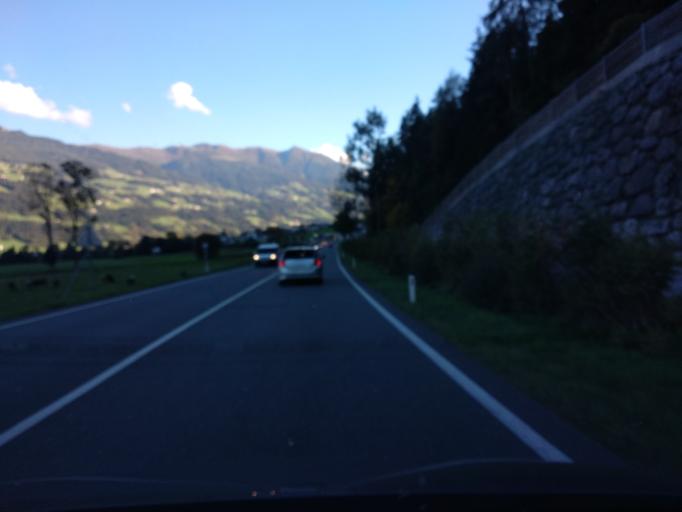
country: AT
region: Tyrol
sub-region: Politischer Bezirk Schwaz
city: Strass im Zillertal
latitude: 47.3850
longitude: 11.8298
